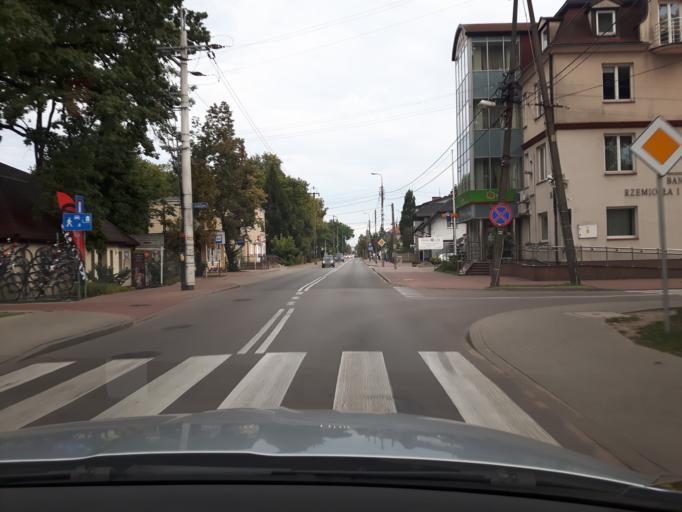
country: PL
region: Masovian Voivodeship
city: Zielonka
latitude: 52.3091
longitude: 21.1542
